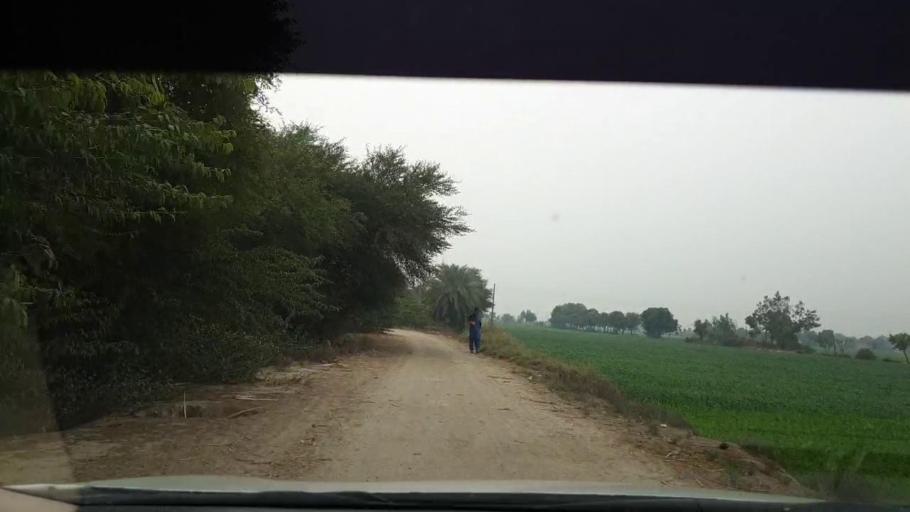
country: PK
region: Sindh
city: Jhol
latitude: 25.8797
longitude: 68.8386
